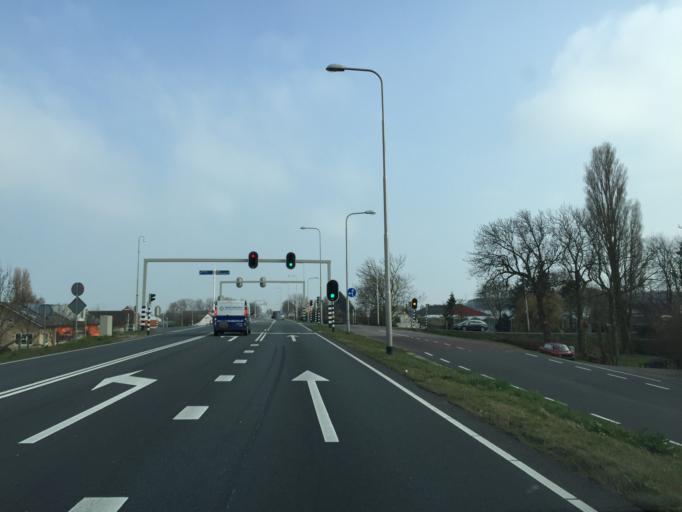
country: NL
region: South Holland
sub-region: Gemeente Westland
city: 's-Gravenzande
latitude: 51.9810
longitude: 4.1790
